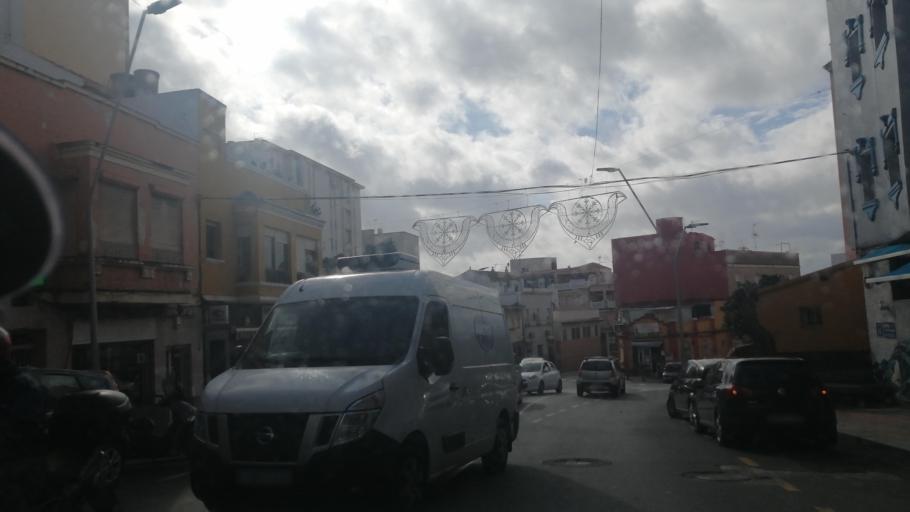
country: ES
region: Ceuta
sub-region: Ceuta
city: Ceuta
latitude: 35.8834
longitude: -5.3281
